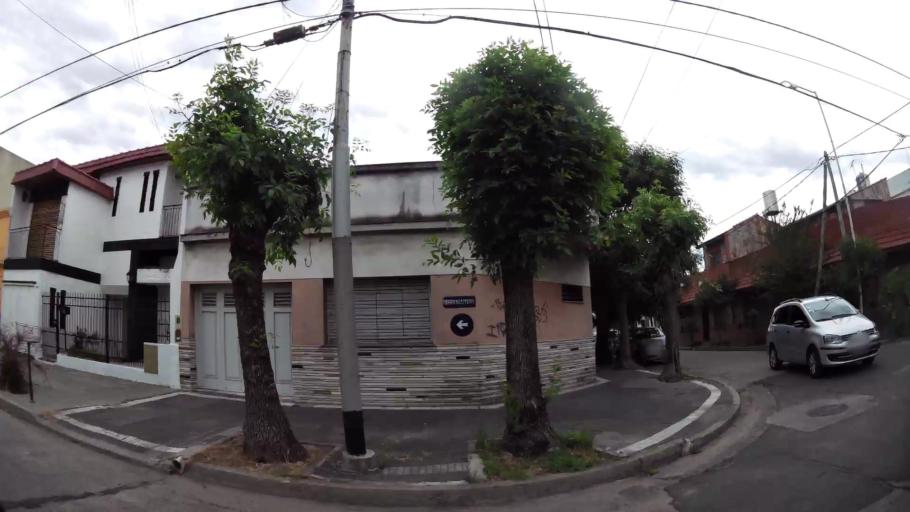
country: AR
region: Buenos Aires
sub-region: Partido de Lanus
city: Lanus
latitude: -34.6828
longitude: -58.3872
